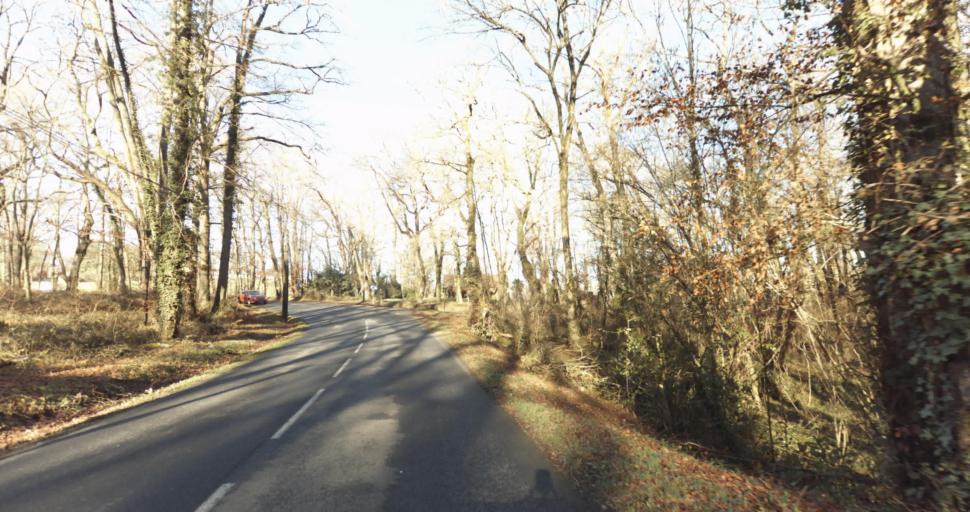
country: FR
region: Aquitaine
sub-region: Departement des Pyrenees-Atlantiques
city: Morlaas
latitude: 43.3392
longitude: -0.2457
